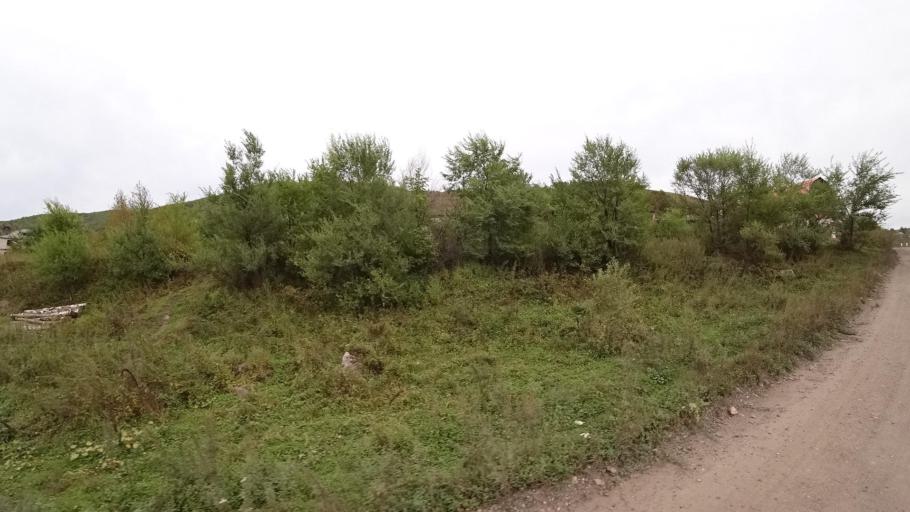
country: RU
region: Jewish Autonomous Oblast
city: Khingansk
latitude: 49.0312
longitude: 131.0566
